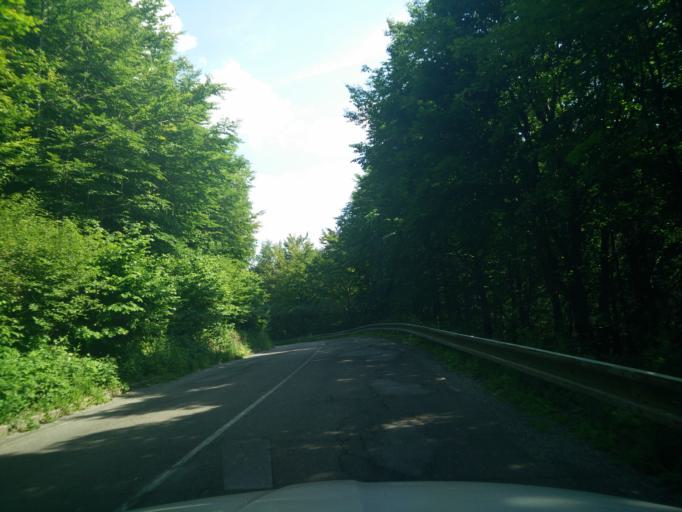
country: SK
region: Zilinsky
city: Rajec
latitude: 48.9588
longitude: 18.6146
